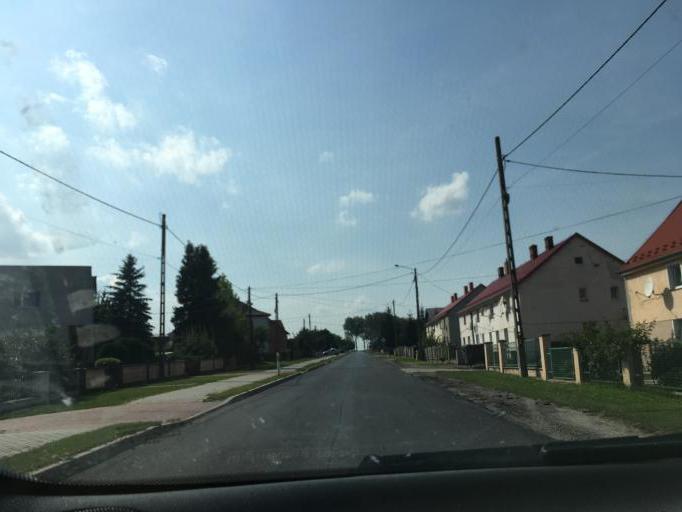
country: PL
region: Opole Voivodeship
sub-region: Powiat prudnicki
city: Raclawice Slaskie
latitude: 50.3105
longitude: 17.7614
